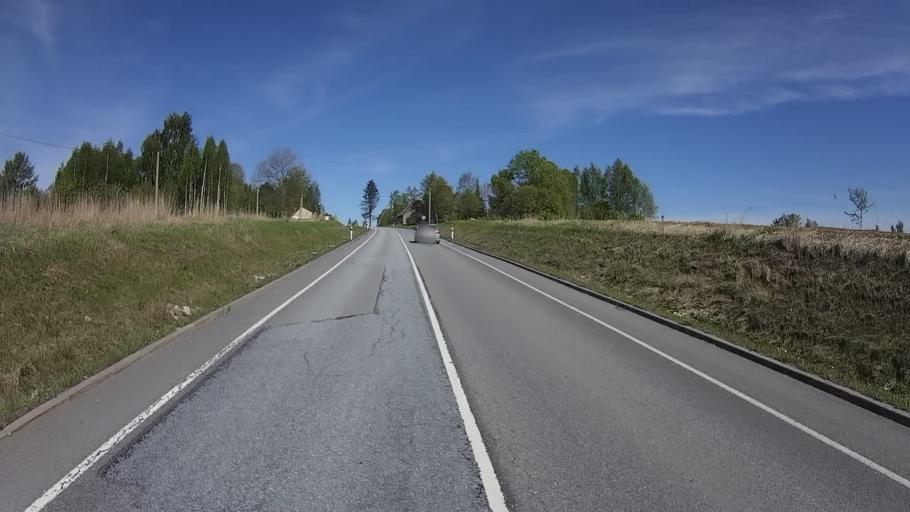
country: RU
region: Pskov
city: Pechory
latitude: 57.8465
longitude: 27.5842
